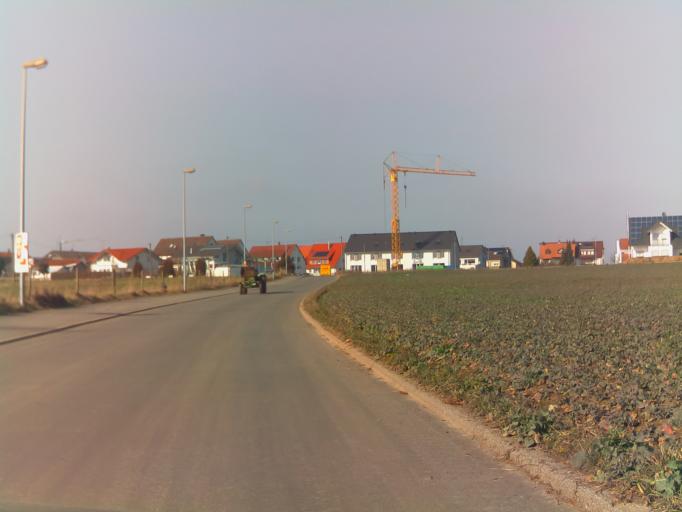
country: DE
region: Baden-Wuerttemberg
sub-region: Regierungsbezirk Stuttgart
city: Ehningen
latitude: 48.6838
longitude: 8.9574
